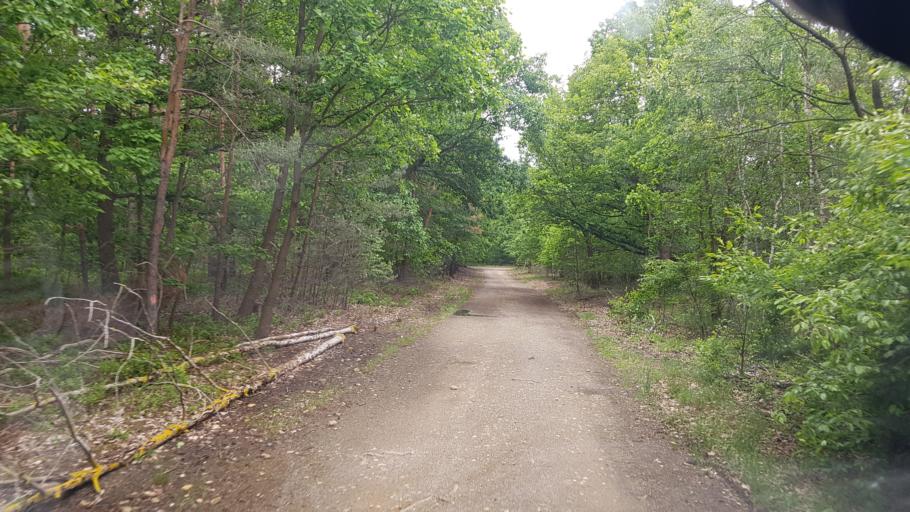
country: DE
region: Brandenburg
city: Hohenleipisch
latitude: 51.5274
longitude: 13.5415
